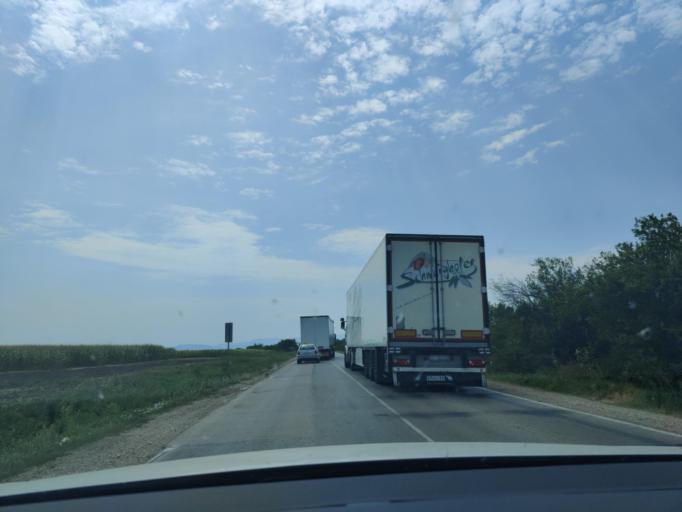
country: BG
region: Vidin
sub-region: Obshtina Ruzhintsi
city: Ruzhintsi
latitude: 43.6723
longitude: 22.7727
